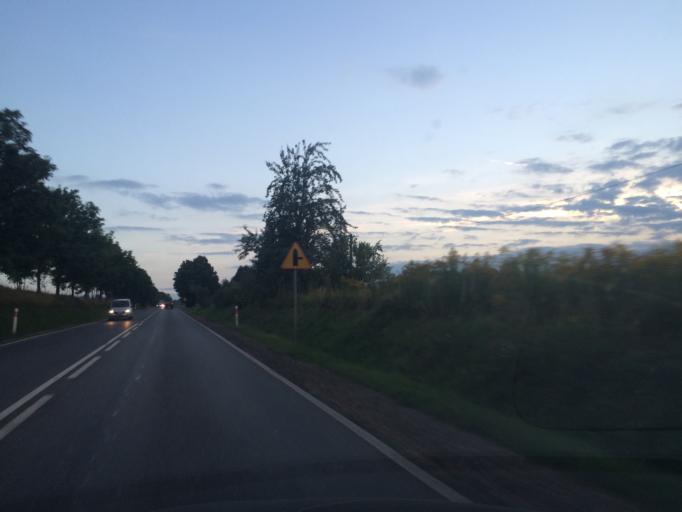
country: PL
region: Swietokrzyskie
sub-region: Powiat starachowicki
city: Wachock
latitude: 51.0727
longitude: 21.0045
